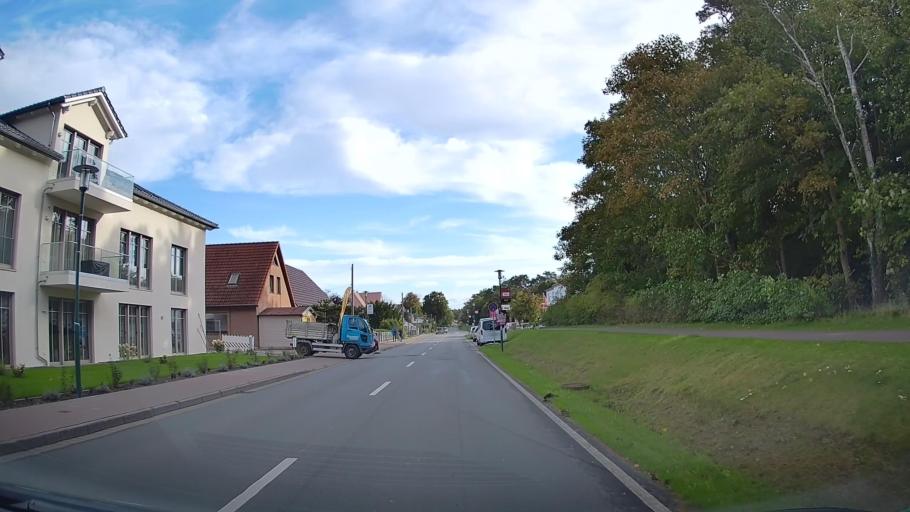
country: DE
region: Mecklenburg-Vorpommern
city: Seeheilbad Graal-Muritz
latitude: 54.2574
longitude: 12.2593
